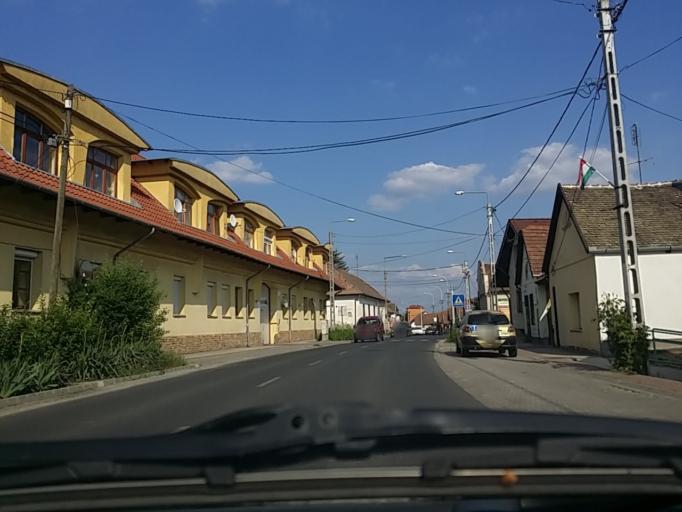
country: HU
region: Pest
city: Nagykovacsi
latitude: 47.6490
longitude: 19.0160
